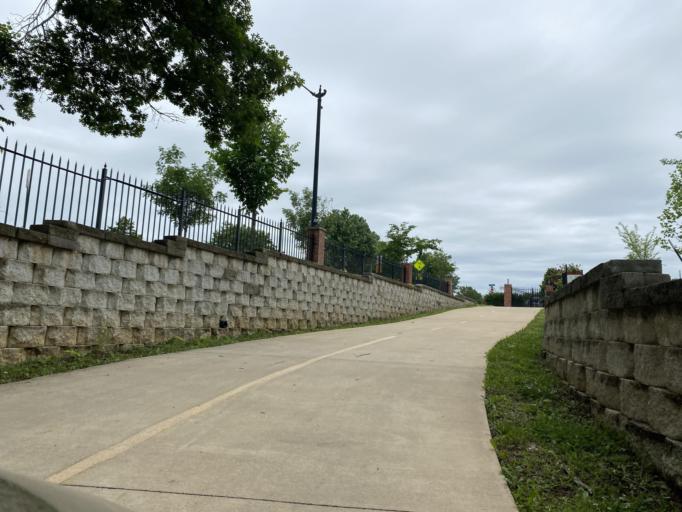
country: US
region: Arkansas
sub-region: Benton County
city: Bentonville
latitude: 36.3656
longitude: -94.2354
